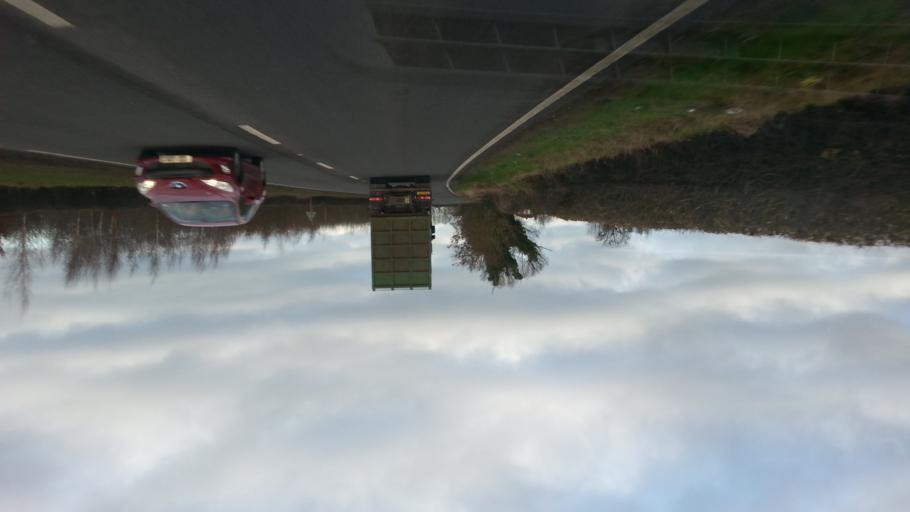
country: GB
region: England
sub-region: Nottinghamshire
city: Newark on Trent
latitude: 53.1104
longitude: -0.8576
